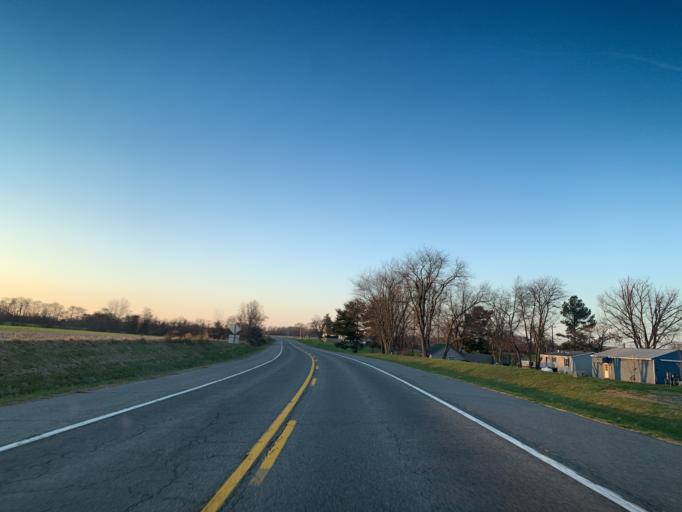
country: US
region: Maryland
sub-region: Cecil County
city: Charlestown
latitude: 39.4259
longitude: -75.9202
